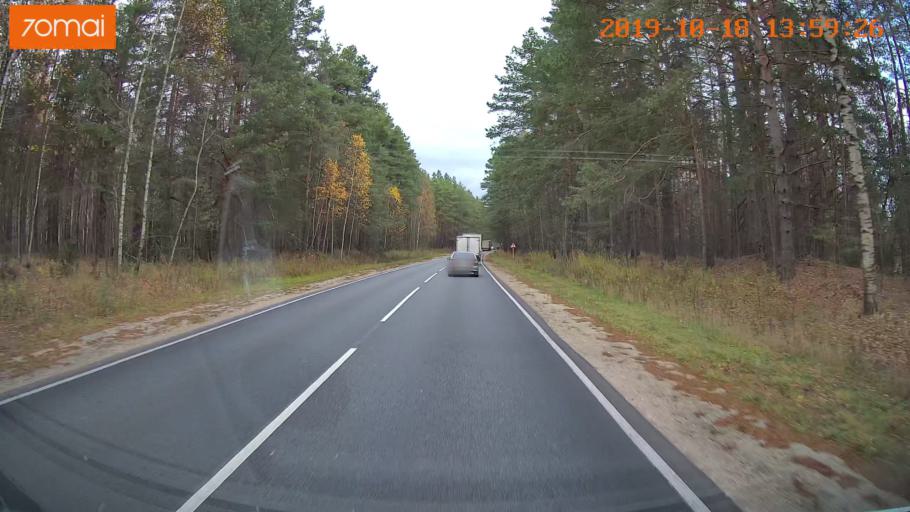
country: RU
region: Rjazan
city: Spas-Klepiki
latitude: 55.0941
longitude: 40.0636
